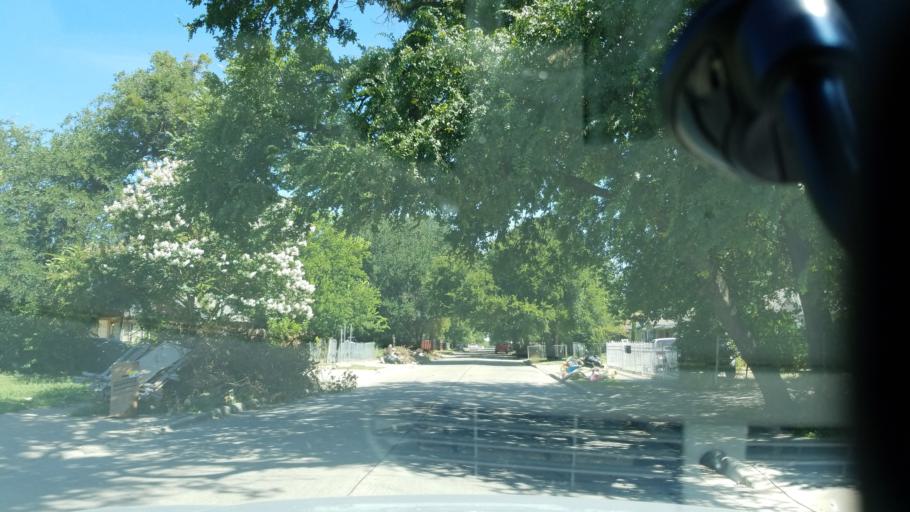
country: US
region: Texas
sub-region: Dallas County
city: Dallas
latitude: 32.7097
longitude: -96.8159
